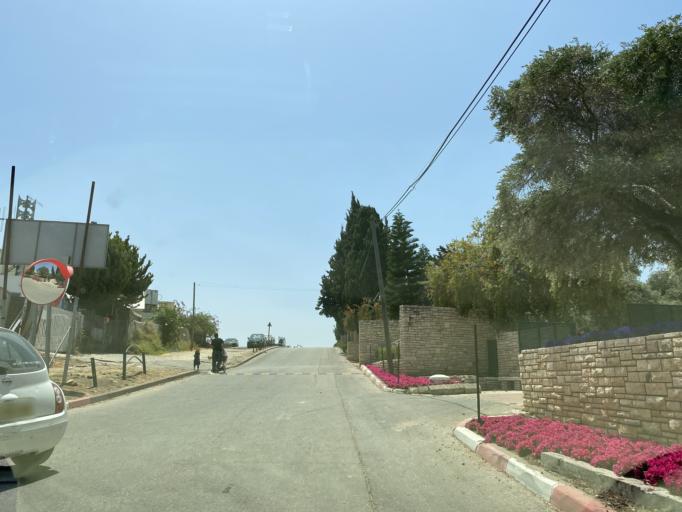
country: IL
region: Tel Aviv
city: Ramat HaSharon
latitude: 32.1305
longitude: 34.8277
